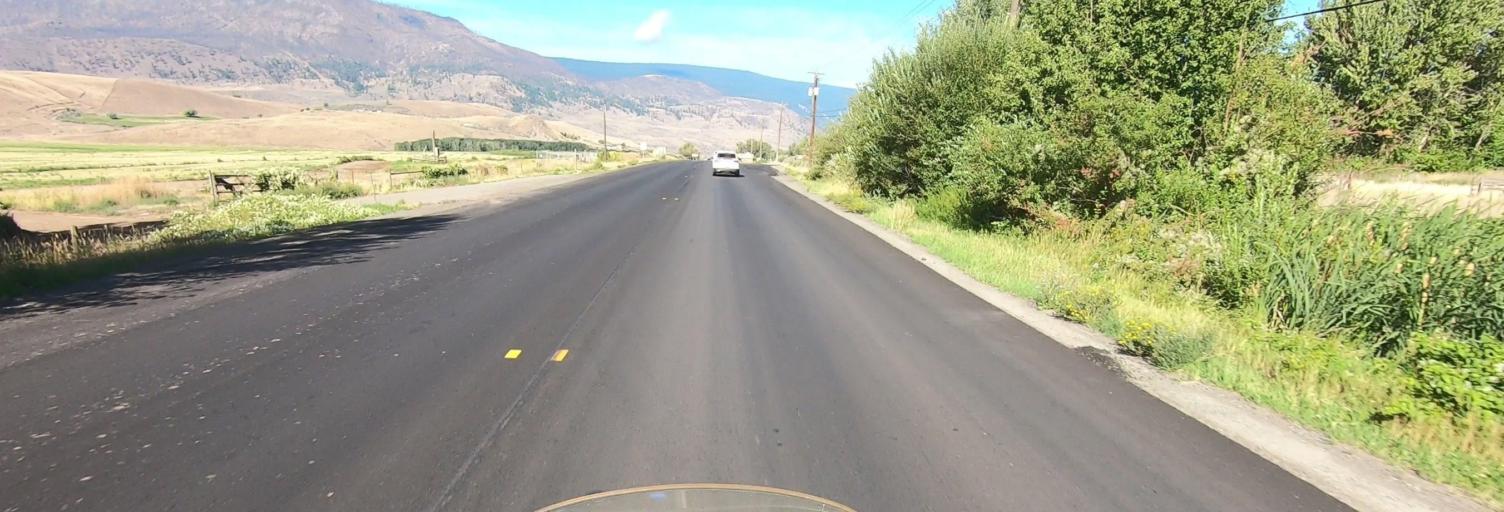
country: CA
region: British Columbia
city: Cache Creek
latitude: 50.8060
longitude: -121.2881
